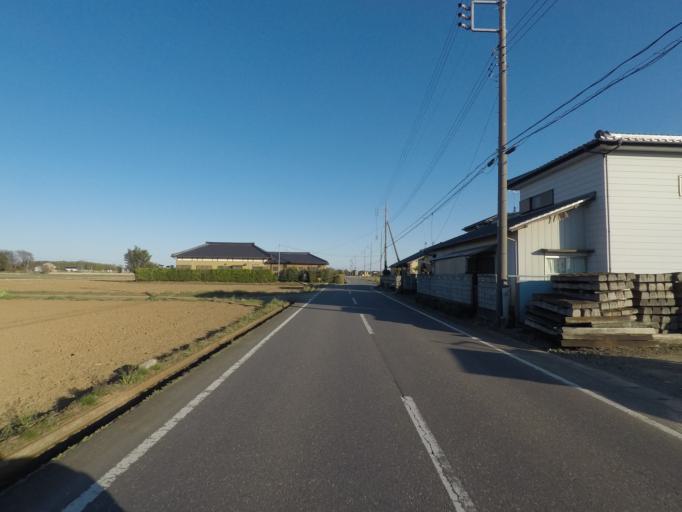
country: JP
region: Ibaraki
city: Ishige
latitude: 36.1321
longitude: 140.0210
